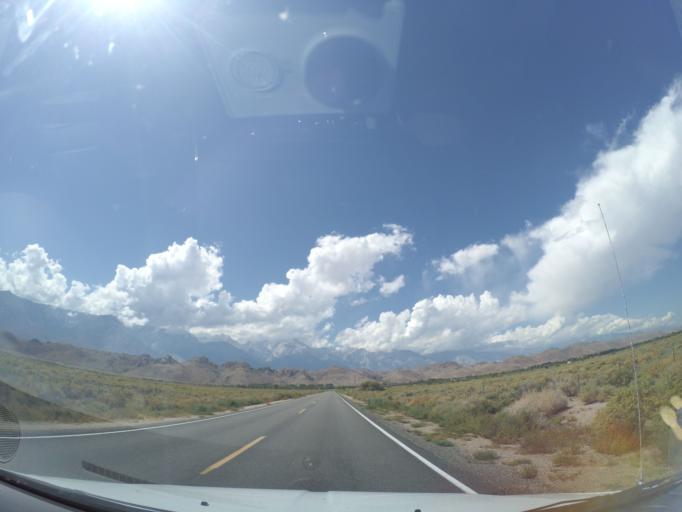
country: US
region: California
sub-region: Inyo County
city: Lone Pine
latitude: 36.5793
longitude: -118.0437
